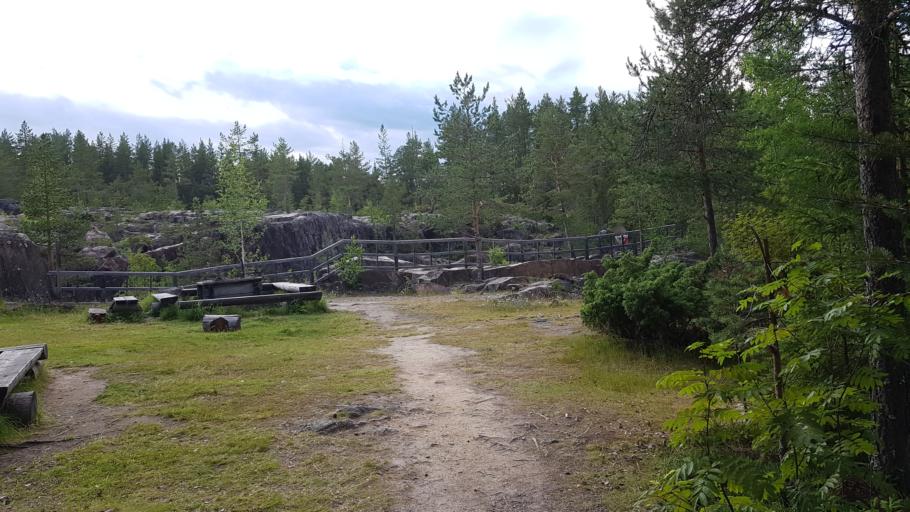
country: SE
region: Norrbotten
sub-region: Alvsbyns Kommun
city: AElvsbyn
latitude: 65.8513
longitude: 20.4070
